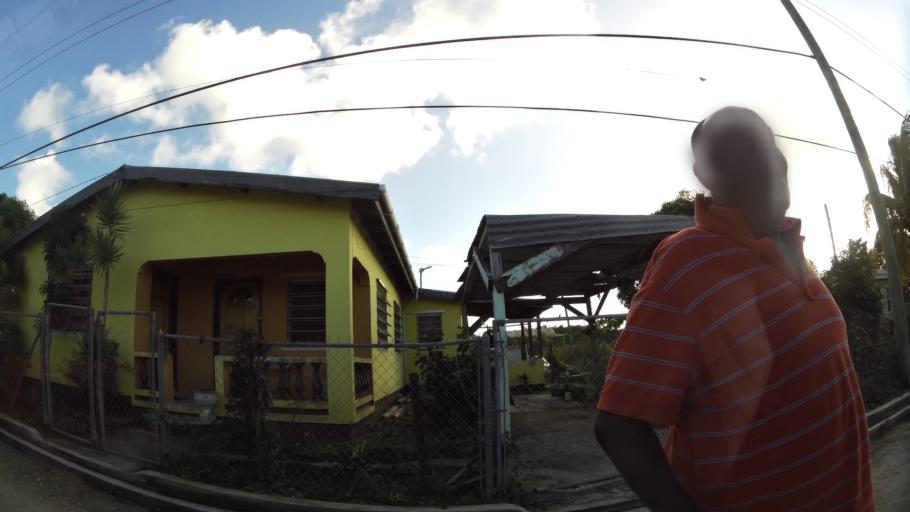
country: AG
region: Saint John
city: Potters Village
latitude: 17.0908
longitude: -61.8039
